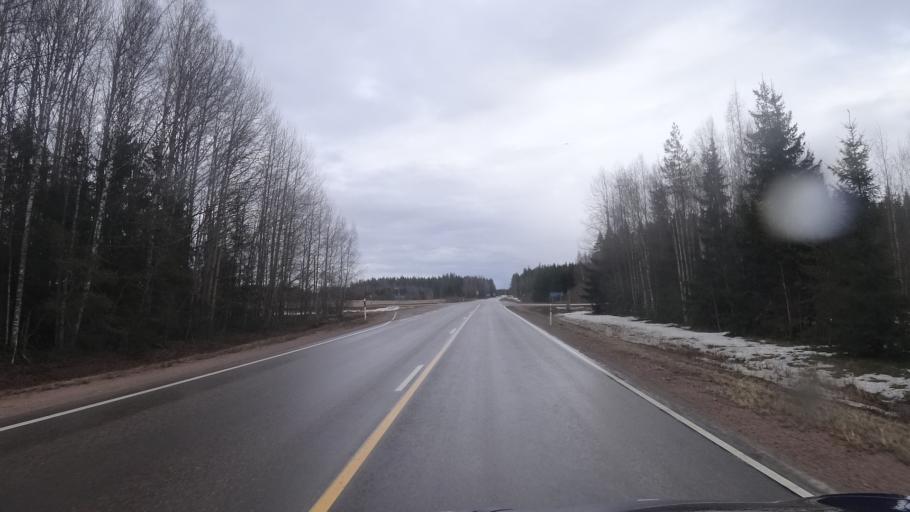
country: FI
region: Kymenlaakso
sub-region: Kouvola
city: Elimaeki
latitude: 60.6907
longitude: 26.5677
